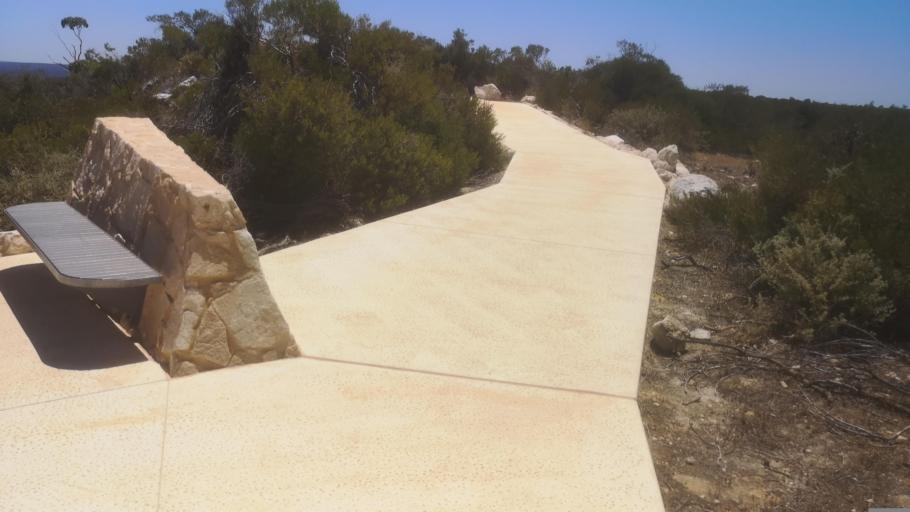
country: AU
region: Western Australia
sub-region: Northampton Shire
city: Kalbarri
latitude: -27.6982
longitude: 114.2162
